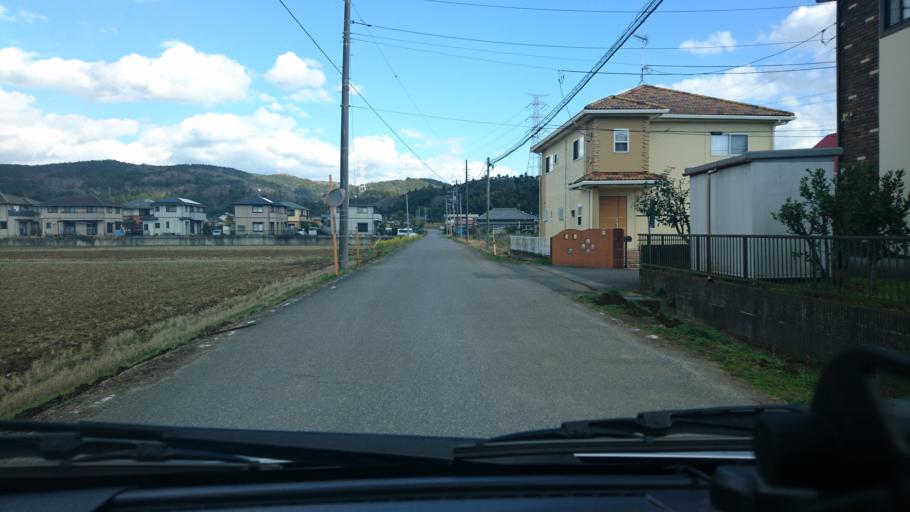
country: JP
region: Chiba
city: Kimitsu
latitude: 35.2873
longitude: 139.9857
